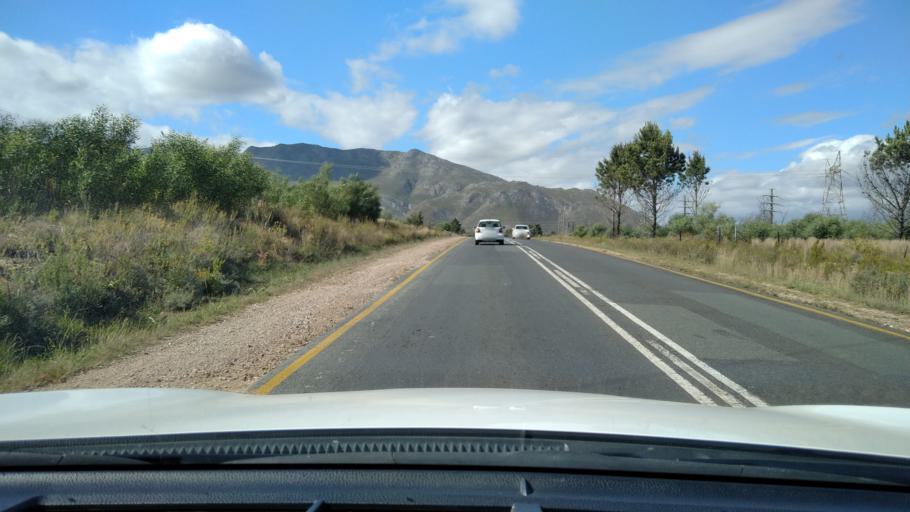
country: ZA
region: Western Cape
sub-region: Overberg District Municipality
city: Hermanus
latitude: -34.2402
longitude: 19.1849
